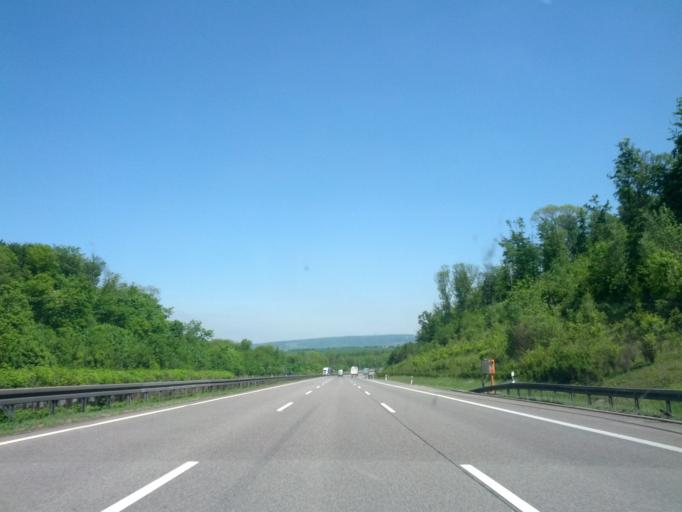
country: DE
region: Thuringia
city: Klettbach
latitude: 50.9332
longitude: 11.1507
